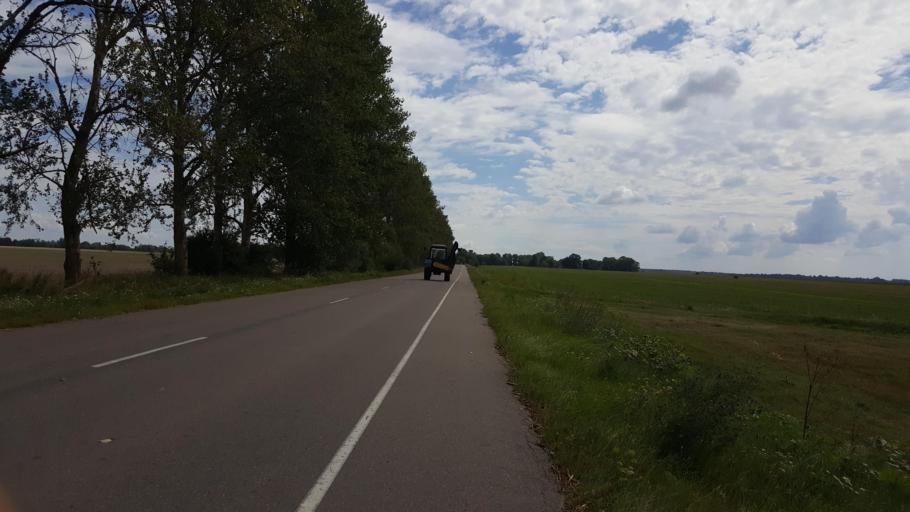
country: BY
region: Brest
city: Zhabinka
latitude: 52.2368
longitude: 23.9894
